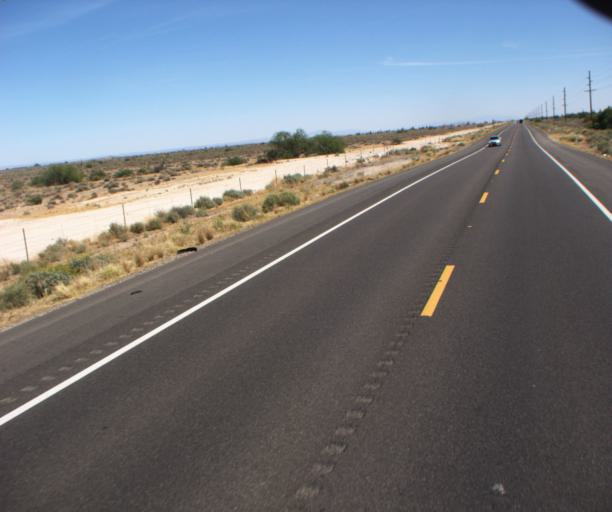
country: US
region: Arizona
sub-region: Pinal County
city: Blackwater
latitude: 33.0377
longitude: -111.6575
